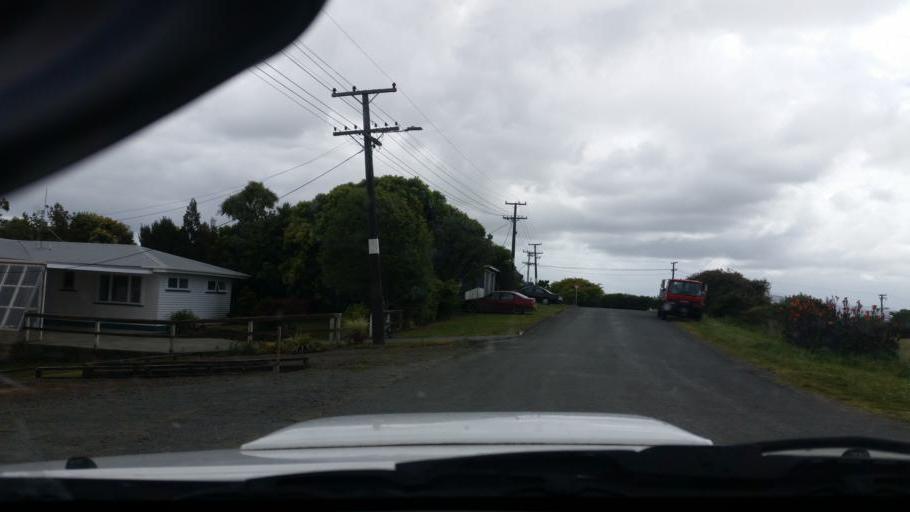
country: NZ
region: Northland
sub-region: Whangarei
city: Ruakaka
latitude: -36.1066
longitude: 174.3477
